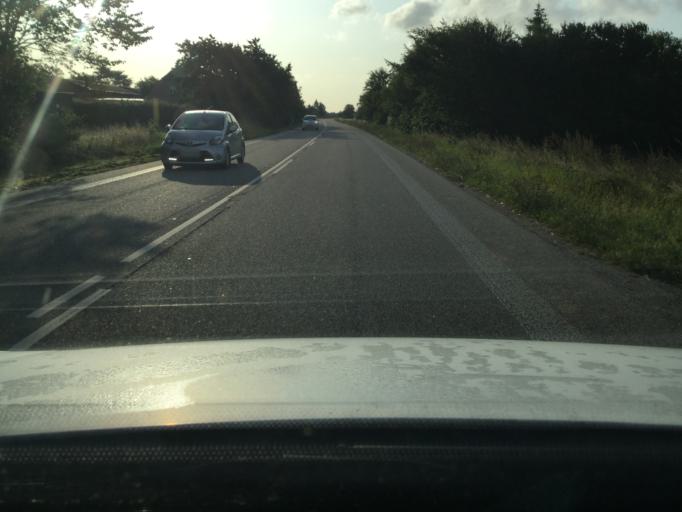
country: DK
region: Zealand
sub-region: Lolland Kommune
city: Rodby
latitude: 54.7654
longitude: 11.3089
